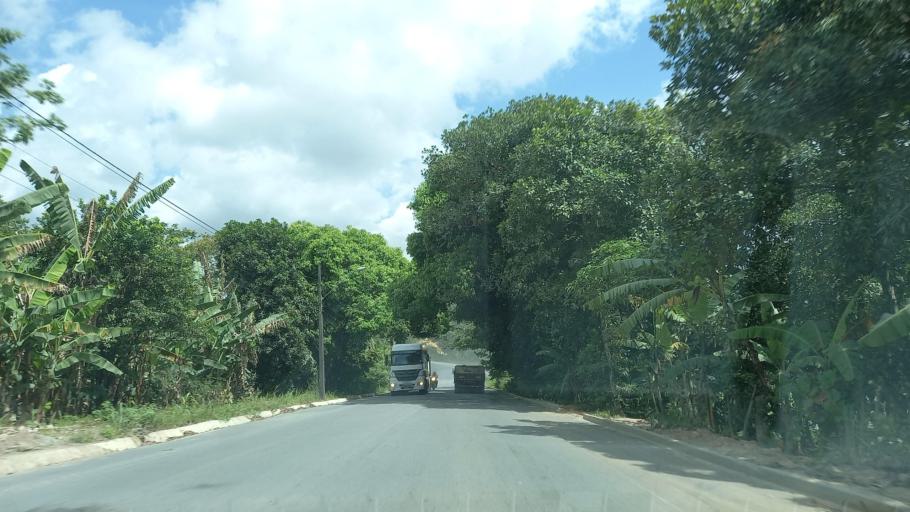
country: BR
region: Pernambuco
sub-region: Jaboatao Dos Guararapes
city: Jaboatao dos Guararapes
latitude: -8.1344
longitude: -35.0044
